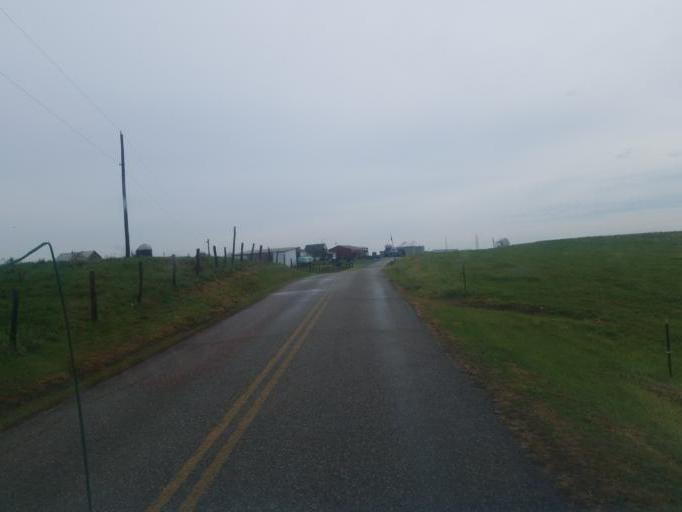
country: US
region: Ohio
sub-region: Washington County
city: Beverly
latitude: 39.5550
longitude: -81.7009
